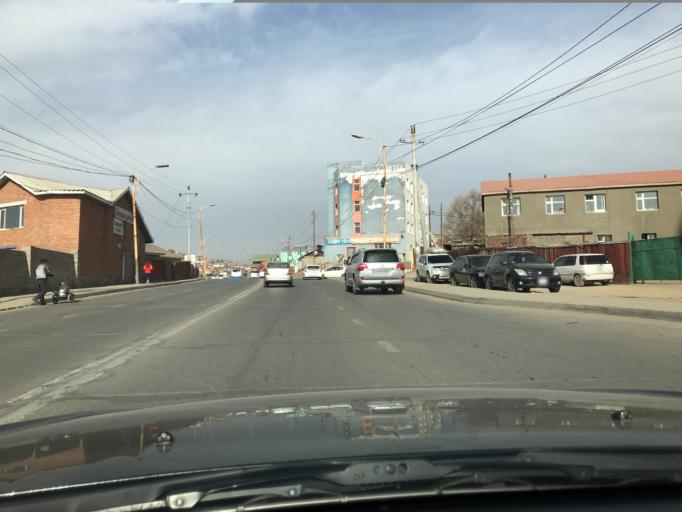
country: MN
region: Ulaanbaatar
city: Ulaanbaatar
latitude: 47.9335
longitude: 106.8868
